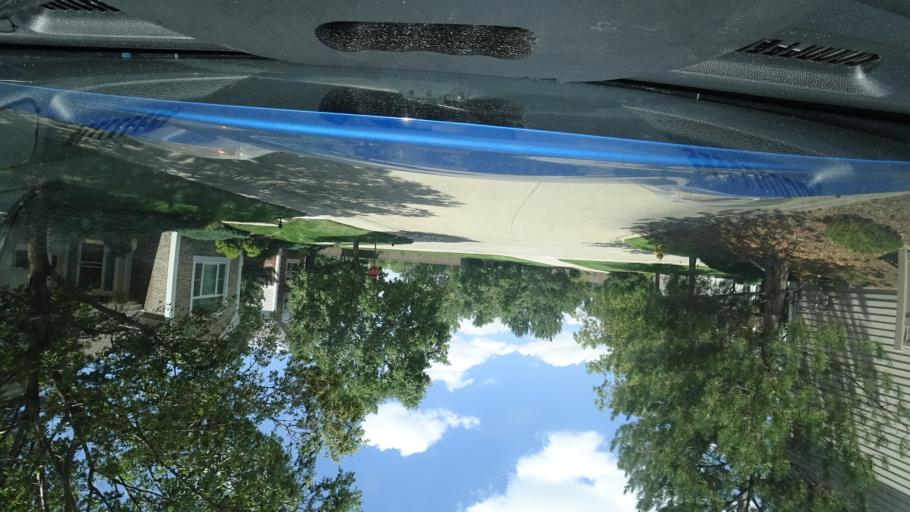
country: US
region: Colorado
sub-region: Arapahoe County
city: Glendale
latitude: 39.6992
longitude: -104.8963
